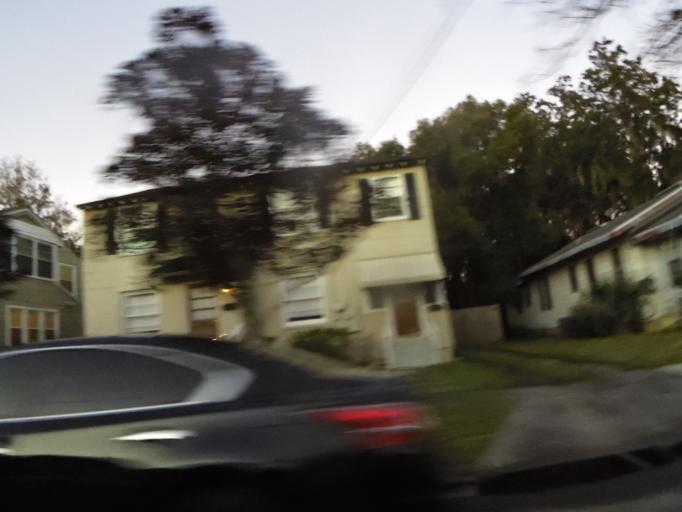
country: US
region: Florida
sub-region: Duval County
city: Jacksonville
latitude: 30.3028
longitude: -81.7110
